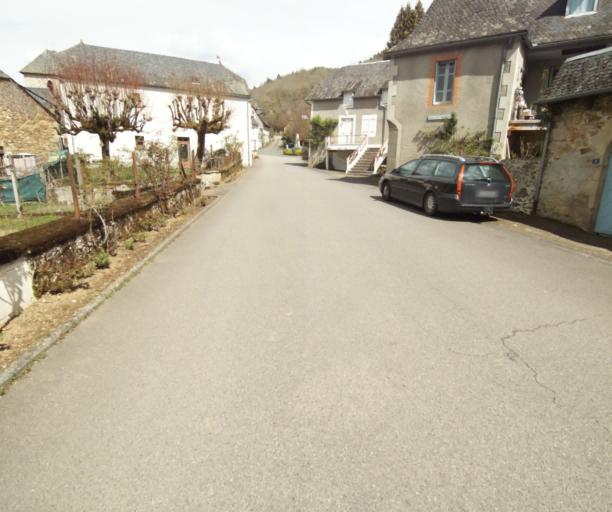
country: FR
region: Limousin
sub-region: Departement de la Correze
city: Argentat
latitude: 45.1753
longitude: 1.8753
